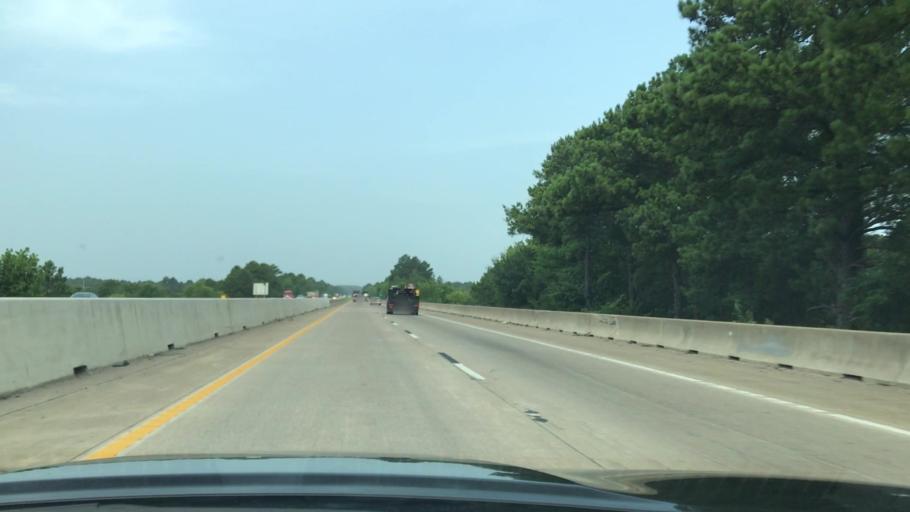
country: US
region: Texas
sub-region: Gregg County
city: Longview
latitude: 32.4424
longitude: -94.7312
